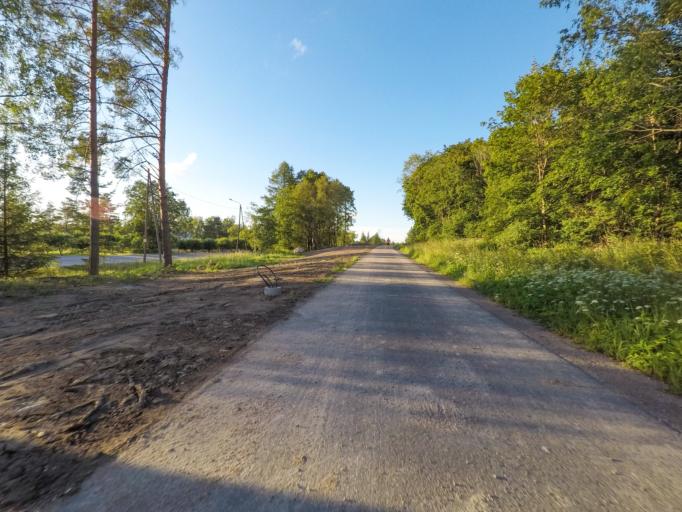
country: FI
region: South Karelia
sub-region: Imatra
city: Imatra
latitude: 61.1994
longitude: 28.7840
